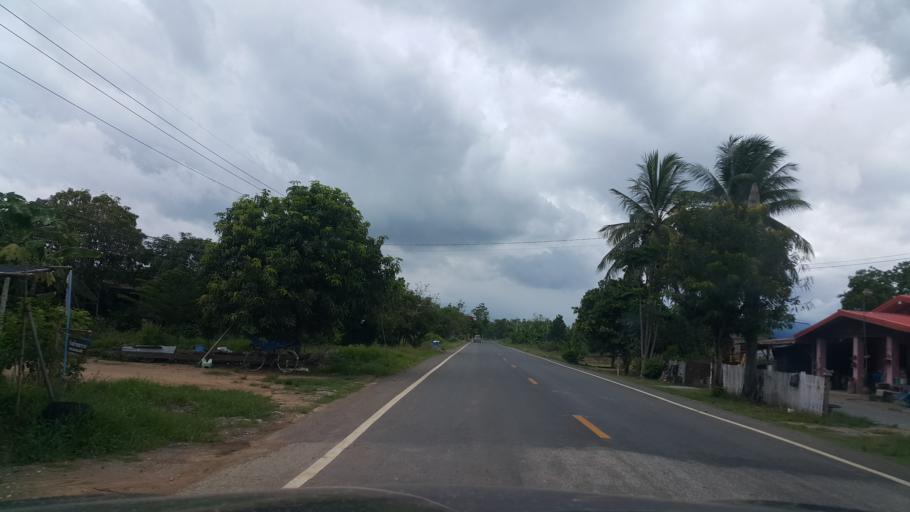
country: TH
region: Sukhothai
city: Sukhothai
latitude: 16.9163
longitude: 99.8707
